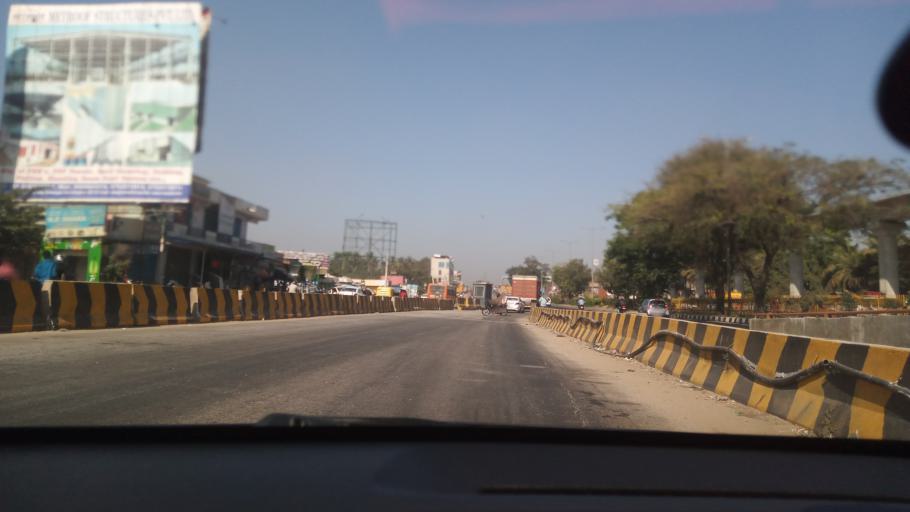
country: IN
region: Karnataka
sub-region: Bangalore Rural
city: Nelamangala
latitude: 13.0571
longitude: 77.4711
